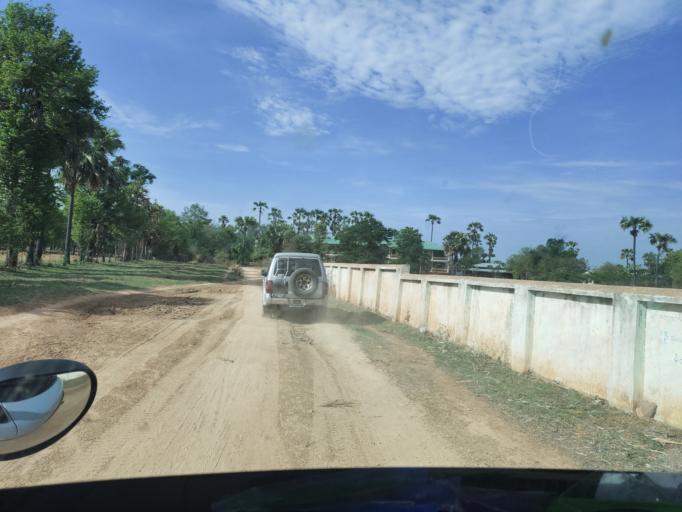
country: MM
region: Magway
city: Chauk
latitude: 20.9589
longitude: 94.9906
